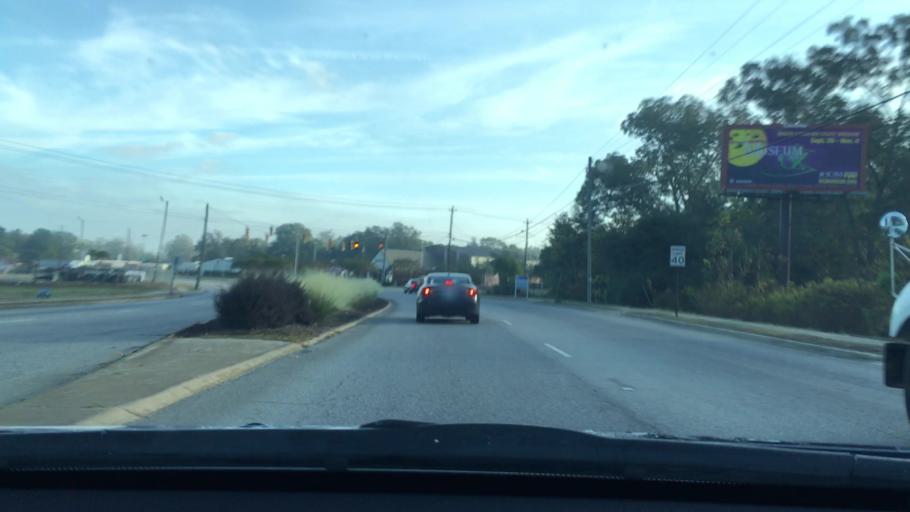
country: US
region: South Carolina
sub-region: Sumter County
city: South Sumter
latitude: 33.8963
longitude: -80.3378
